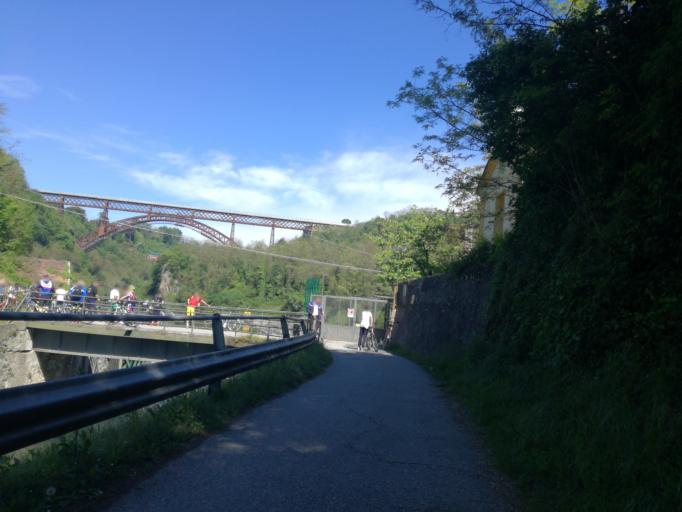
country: IT
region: Lombardy
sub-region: Provincia di Lecco
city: Paderno d'Adda
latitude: 45.6799
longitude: 9.4574
